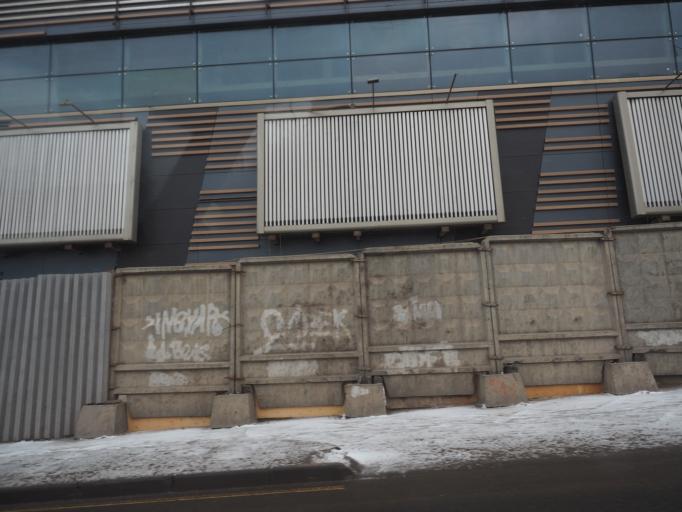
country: RU
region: Moskovskaya
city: Kastanayevo
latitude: 55.7145
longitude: 37.5039
